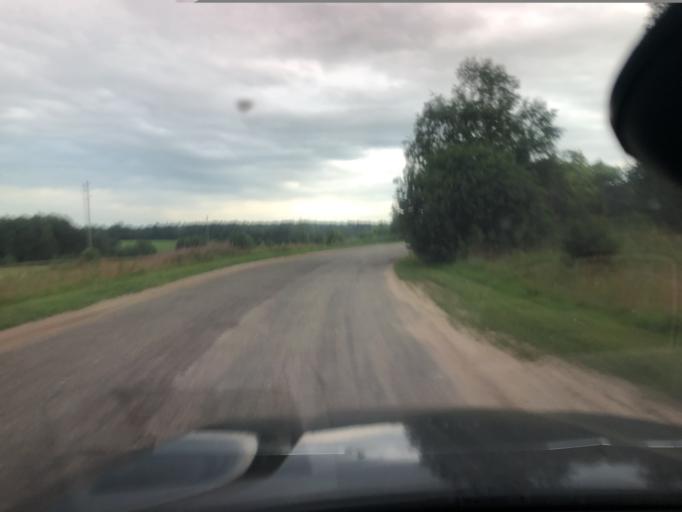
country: RU
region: Jaroslavl
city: Pereslavl'-Zalesskiy
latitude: 57.0316
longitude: 38.9127
